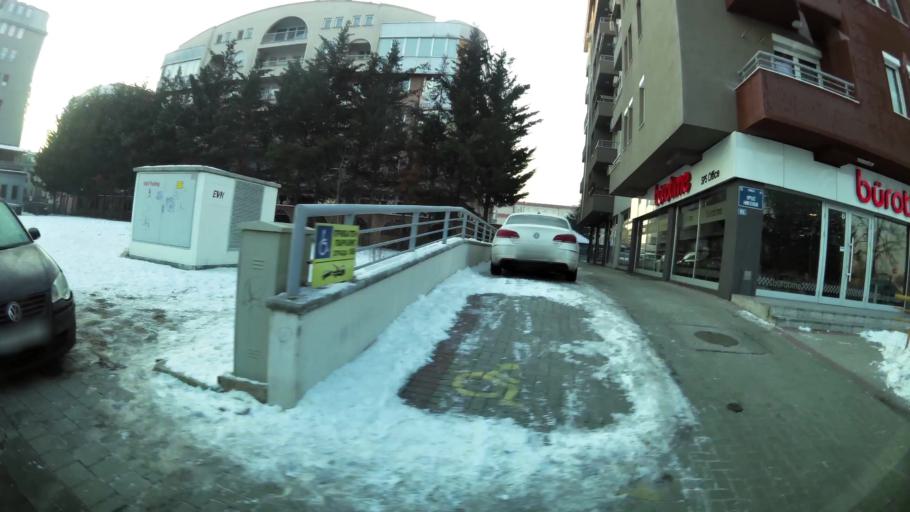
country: MK
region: Karpos
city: Skopje
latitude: 42.0066
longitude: 21.4085
